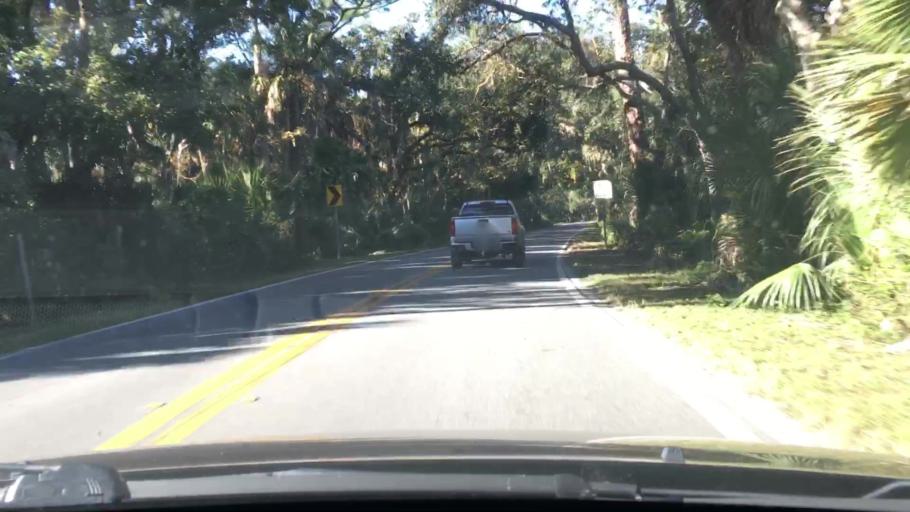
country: US
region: Florida
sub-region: Volusia County
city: Ormond-by-the-Sea
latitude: 29.3451
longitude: -81.0936
